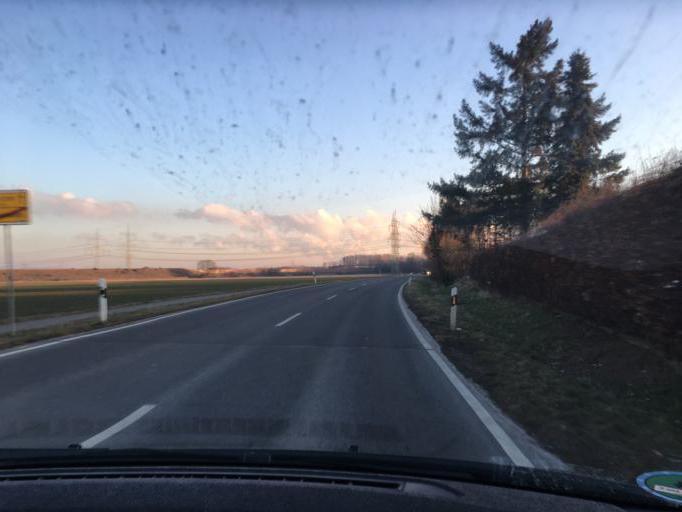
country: DE
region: North Rhine-Westphalia
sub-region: Regierungsbezirk Koln
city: Dueren
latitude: 50.8439
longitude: 6.4867
